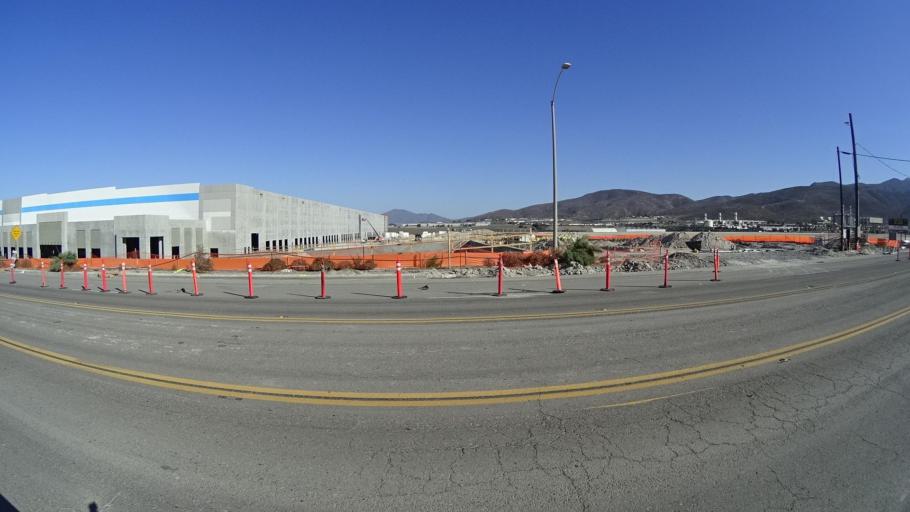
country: MX
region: Baja California
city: Tijuana
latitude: 32.5673
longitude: -116.9238
